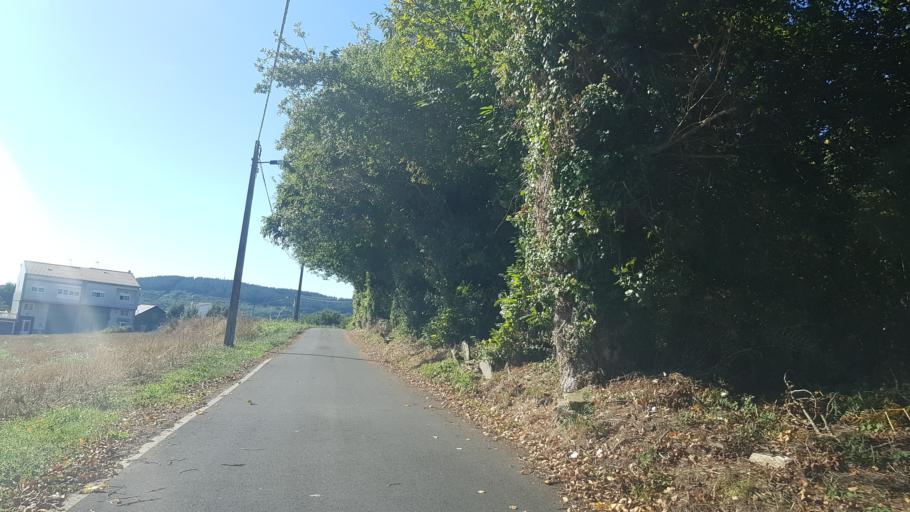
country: ES
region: Galicia
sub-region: Provincia de Lugo
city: Lugo
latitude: 43.0126
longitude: -7.5776
